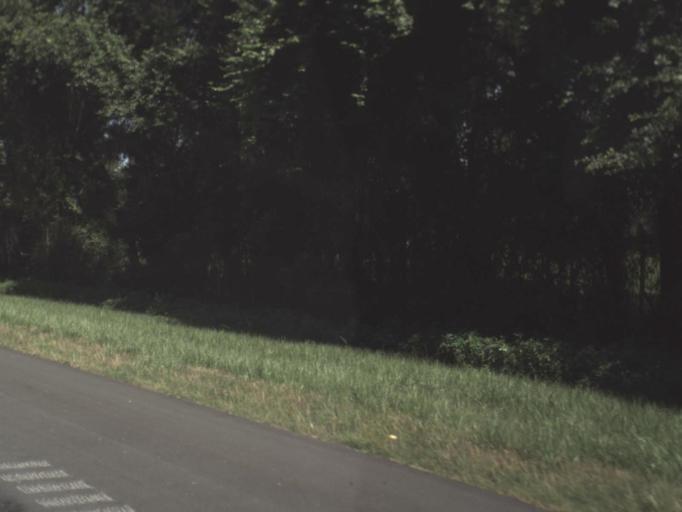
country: US
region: Florida
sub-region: Madison County
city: Madison
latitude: 30.4076
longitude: -83.4070
